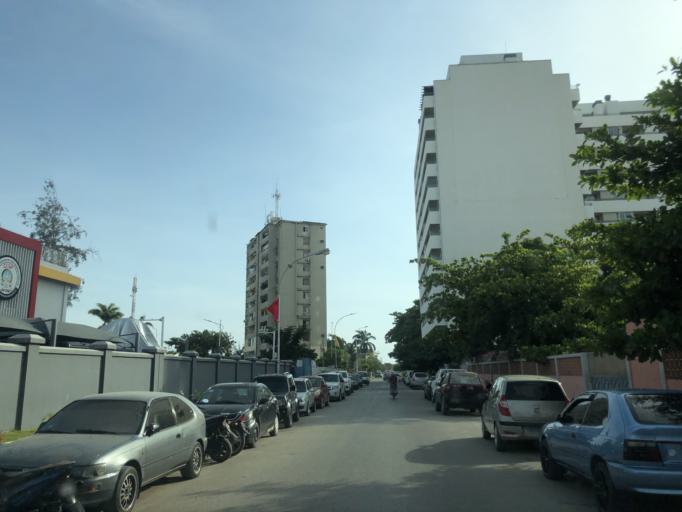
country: AO
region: Benguela
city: Benguela
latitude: -12.5787
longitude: 13.3963
